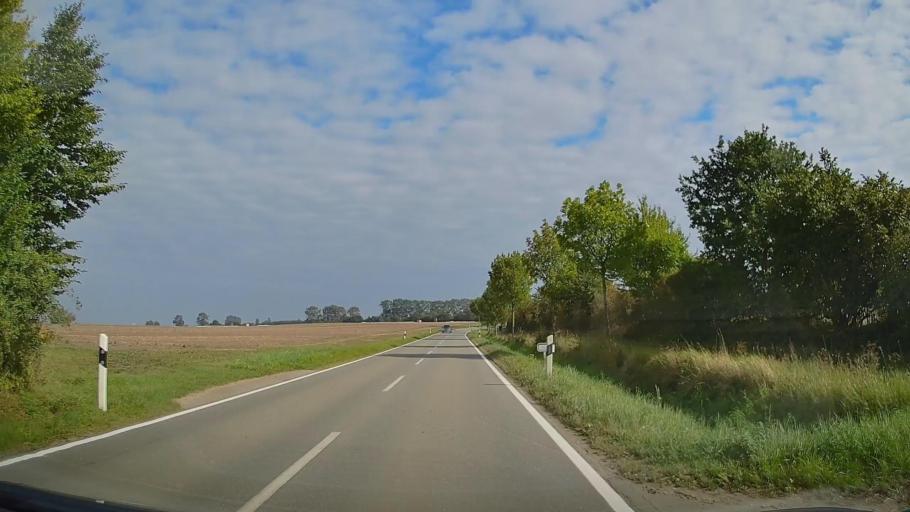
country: DE
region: Schleswig-Holstein
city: Gremersdorf
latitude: 54.3529
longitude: 10.9211
